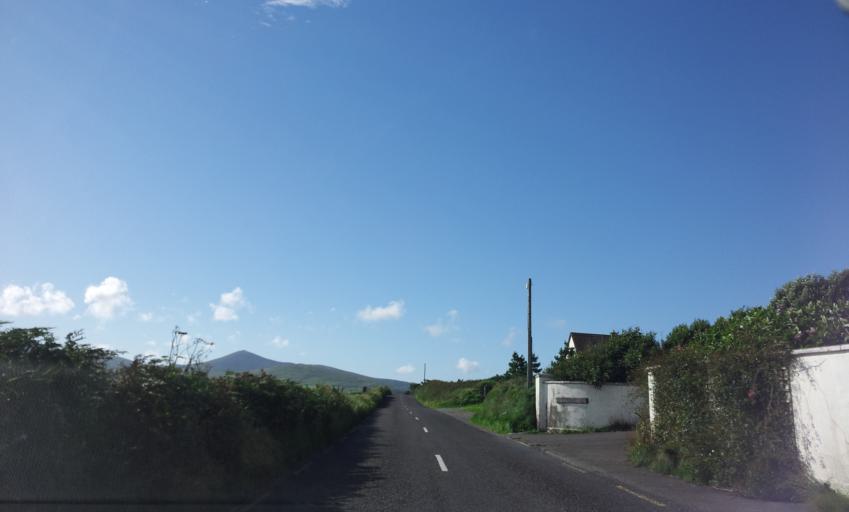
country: IE
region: Munster
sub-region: Ciarrai
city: Dingle
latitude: 52.1261
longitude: -10.3382
